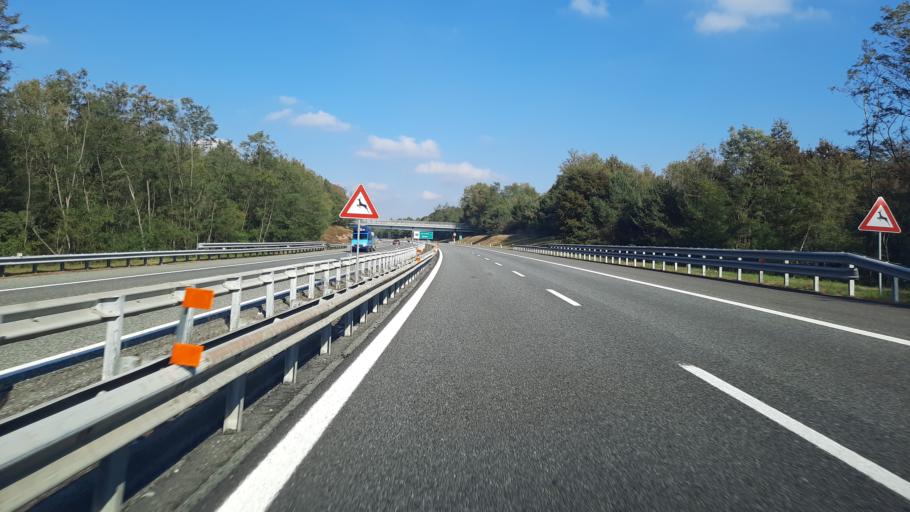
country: IT
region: Piedmont
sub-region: Provincia di Novara
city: Ghemme
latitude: 45.6211
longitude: 8.4391
